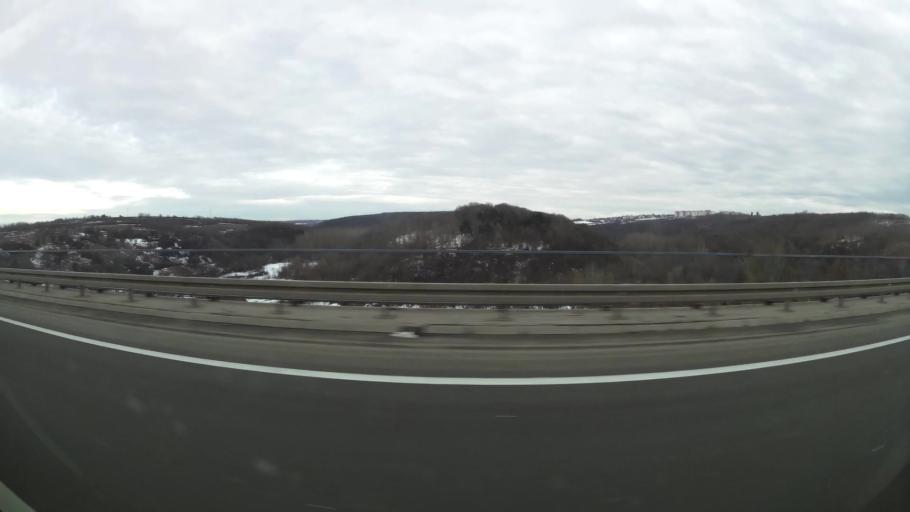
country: RS
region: Central Serbia
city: Sremcica
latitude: 44.7115
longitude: 20.3810
